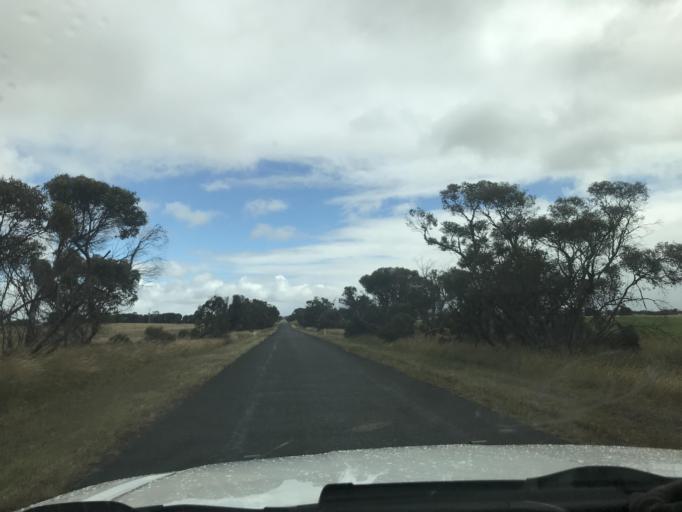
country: AU
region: South Australia
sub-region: Tatiara
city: Bordertown
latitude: -36.2239
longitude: 141.1575
